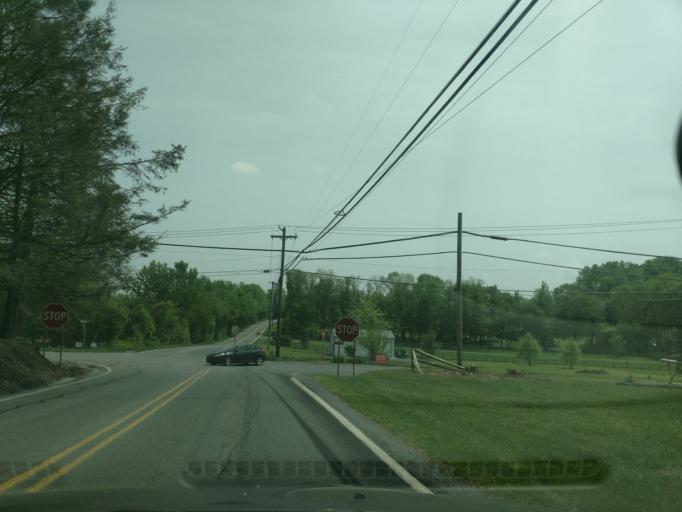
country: US
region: Pennsylvania
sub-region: Chester County
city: Elverson
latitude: 40.1743
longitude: -75.8539
